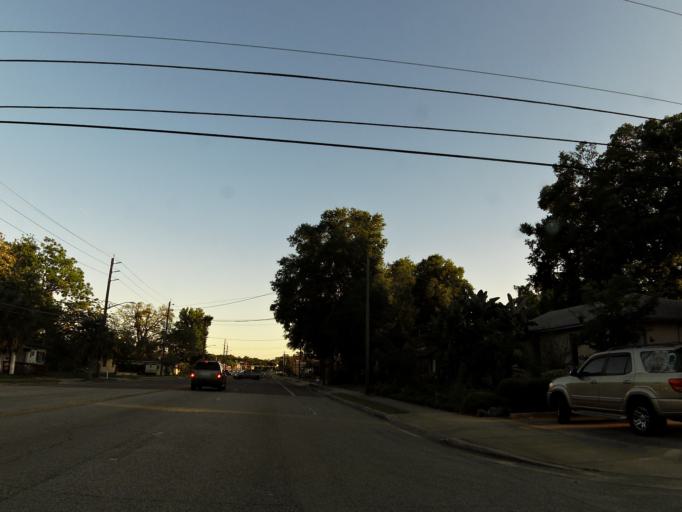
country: US
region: Florida
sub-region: Duval County
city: Jacksonville
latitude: 30.3173
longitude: -81.5795
